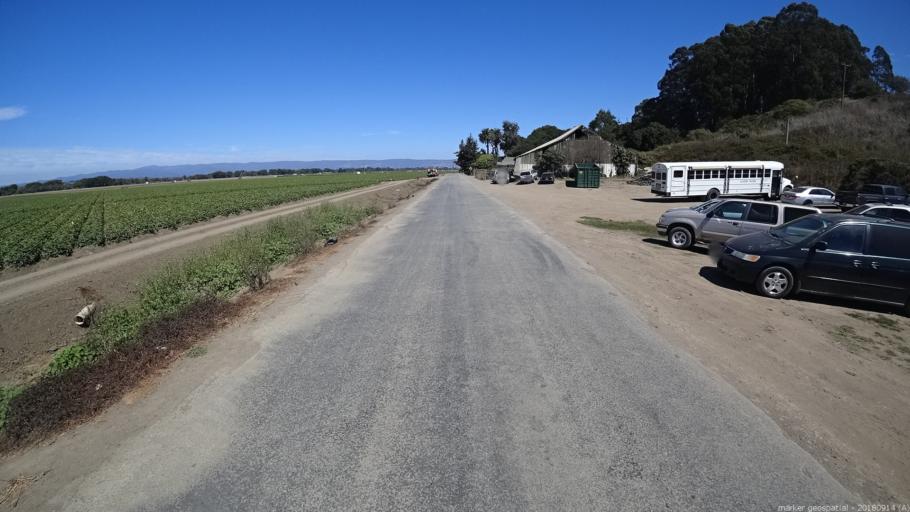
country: US
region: California
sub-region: Santa Cruz County
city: Watsonville
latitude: 36.8651
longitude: -121.7973
